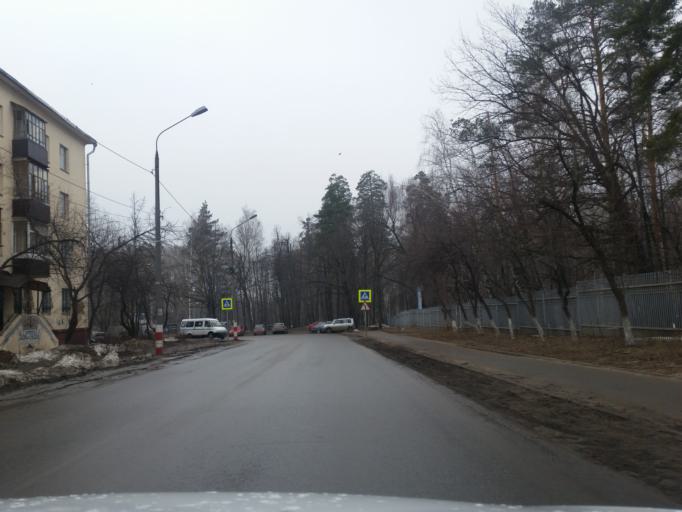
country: RU
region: Ulyanovsk
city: Dimitrovgrad
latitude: 54.2248
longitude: 49.5435
